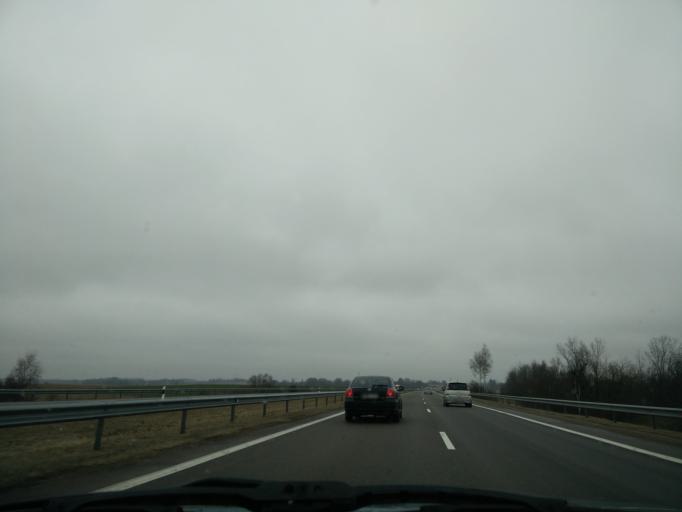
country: LT
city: Skaudvile
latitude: 55.4387
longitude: 22.7333
